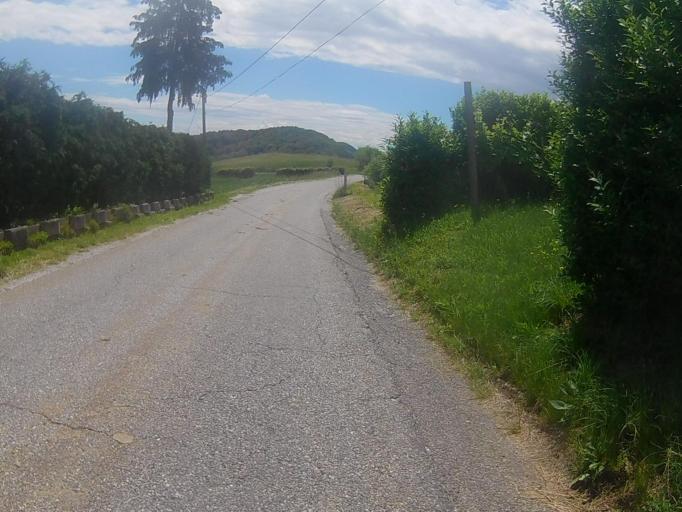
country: SI
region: Duplek
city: Zgornji Duplek
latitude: 46.5493
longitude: 15.7245
